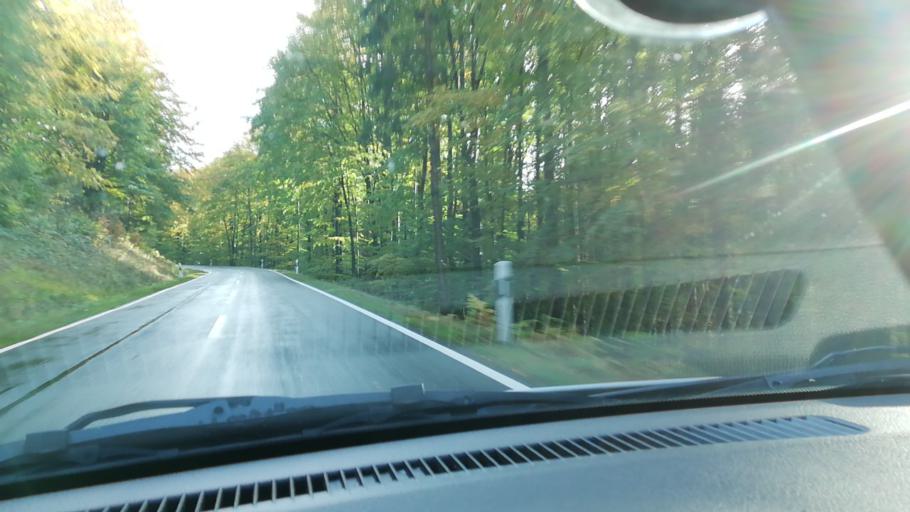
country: DE
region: Bavaria
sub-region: Regierungsbezirk Unterfranken
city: Neuhutten
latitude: 49.9860
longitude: 9.4589
